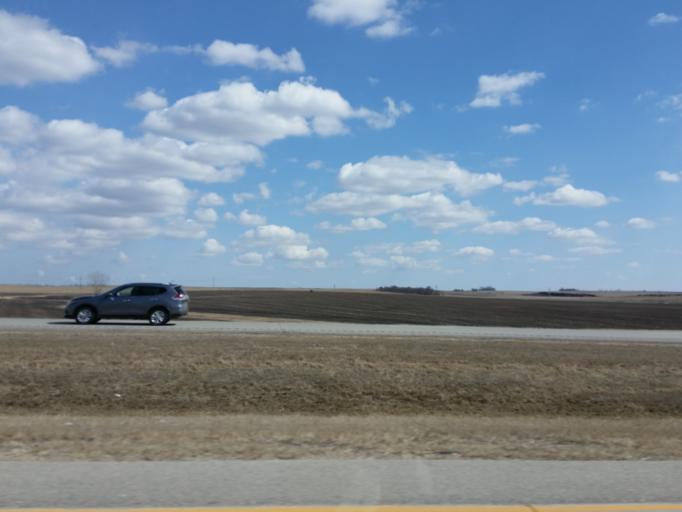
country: US
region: South Dakota
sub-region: Codington County
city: Watertown
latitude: 45.0024
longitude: -97.0546
